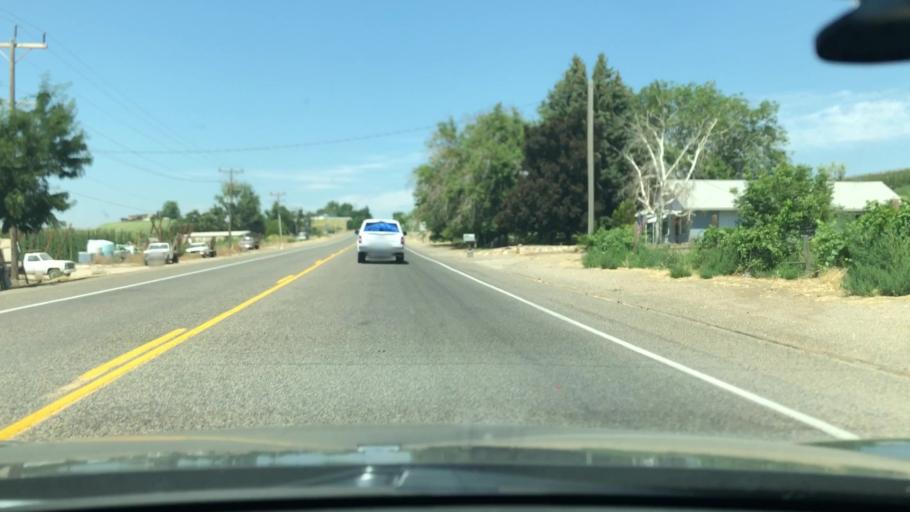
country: US
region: Idaho
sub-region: Canyon County
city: Wilder
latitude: 43.6541
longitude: -116.9118
